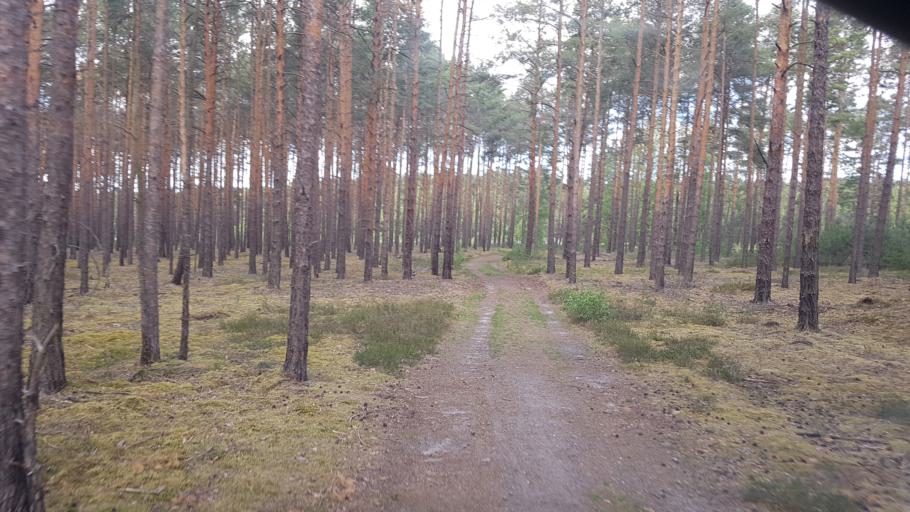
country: DE
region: Brandenburg
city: Finsterwalde
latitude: 51.6424
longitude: 13.6623
